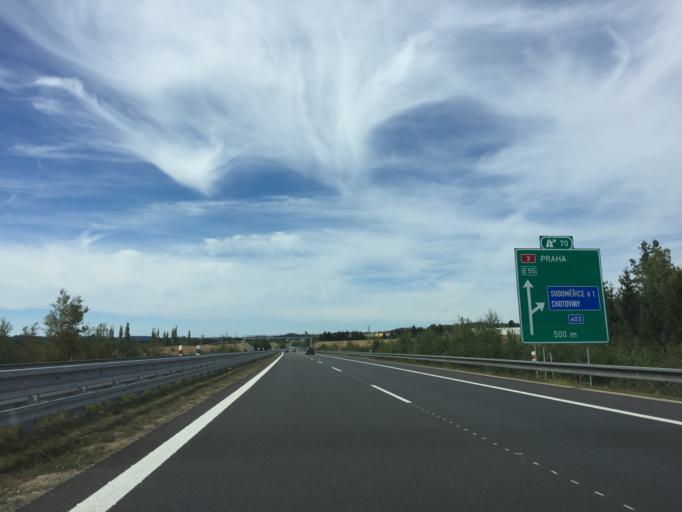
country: CZ
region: Jihocesky
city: Chotoviny
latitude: 49.4636
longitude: 14.6644
